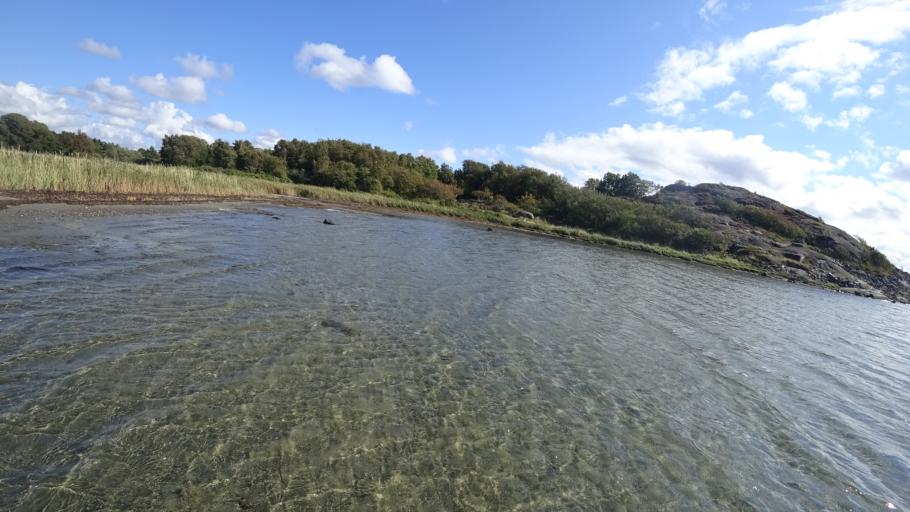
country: SE
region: Vaestra Goetaland
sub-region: Goteborg
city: Styrso
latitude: 57.6018
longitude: 11.7776
